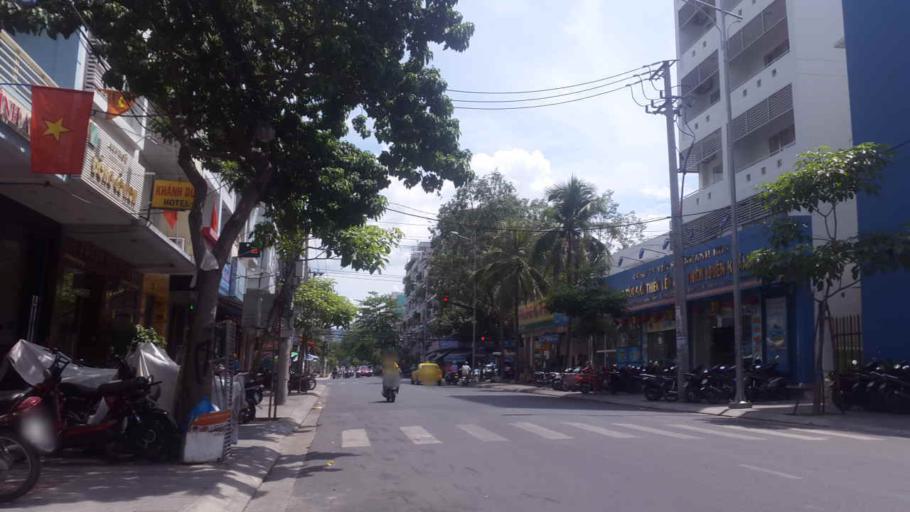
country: VN
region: Khanh Hoa
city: Nha Trang
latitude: 12.2451
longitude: 109.1940
